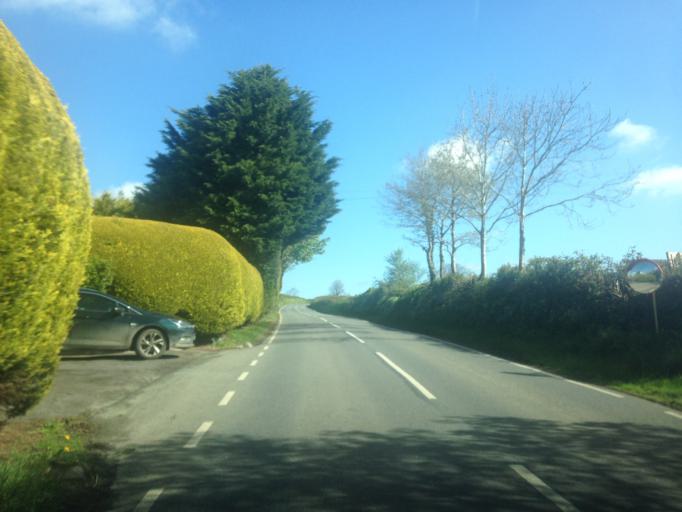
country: GB
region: Wales
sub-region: County of Ceredigion
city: Newcastle Emlyn
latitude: 52.0662
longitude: -4.4363
